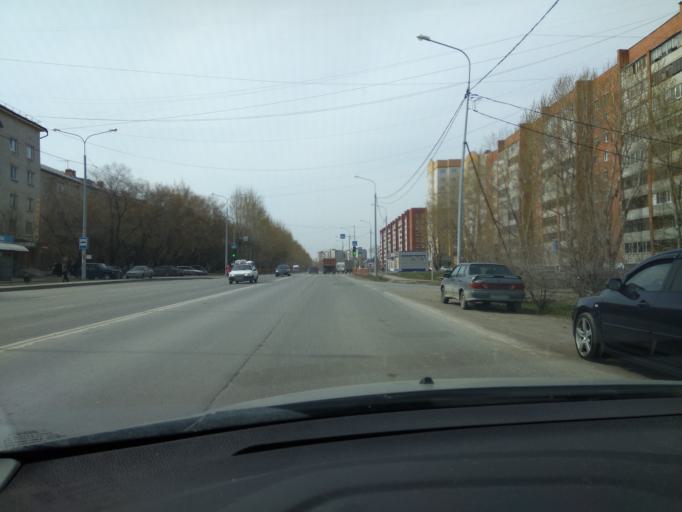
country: RU
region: Tjumen
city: Melioratorov
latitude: 57.1877
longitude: 65.5916
